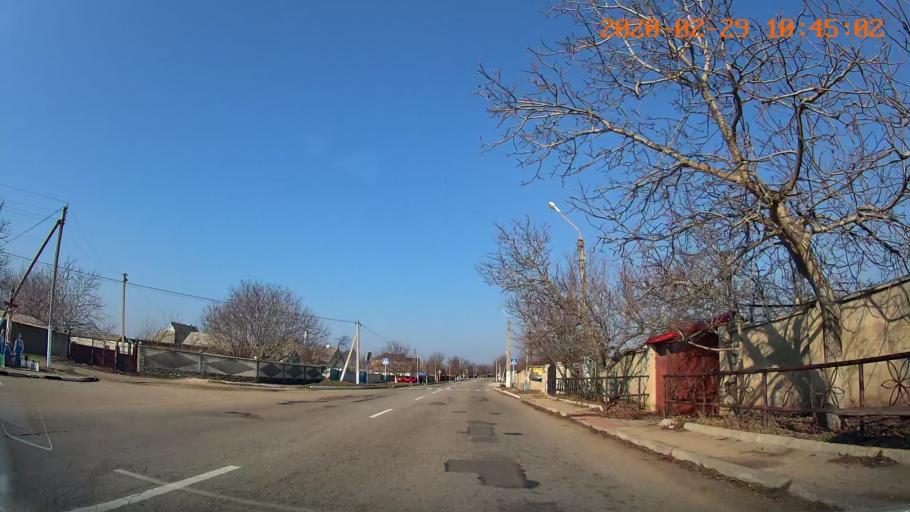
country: MD
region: Telenesti
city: Grigoriopol
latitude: 47.0733
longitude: 29.3875
